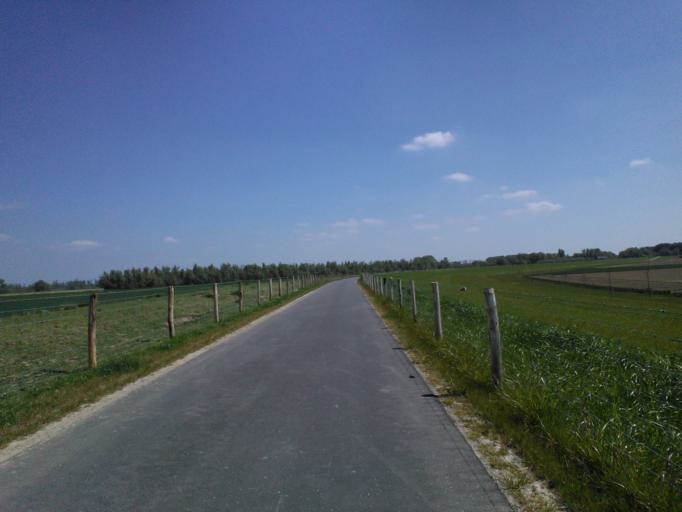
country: NL
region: South Holland
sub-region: Gemeente Sliedrecht
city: Sliedrecht
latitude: 51.7959
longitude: 4.7491
